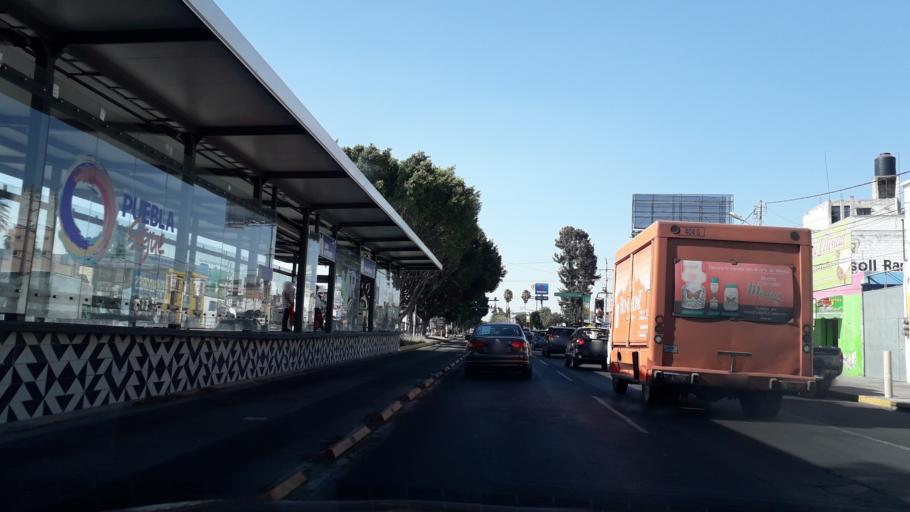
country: MX
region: Puebla
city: Puebla
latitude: 19.0560
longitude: -98.1929
